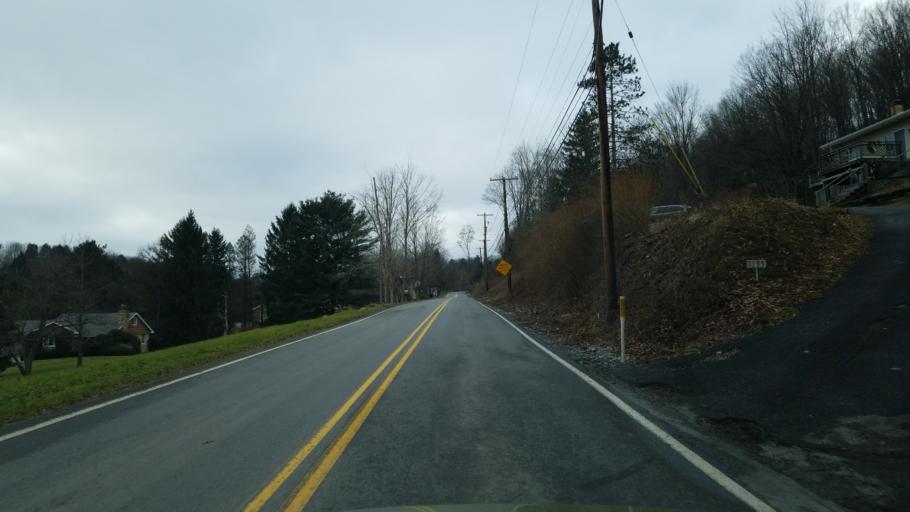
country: US
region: Pennsylvania
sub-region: Clearfield County
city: Clearfield
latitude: 41.0304
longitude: -78.4561
